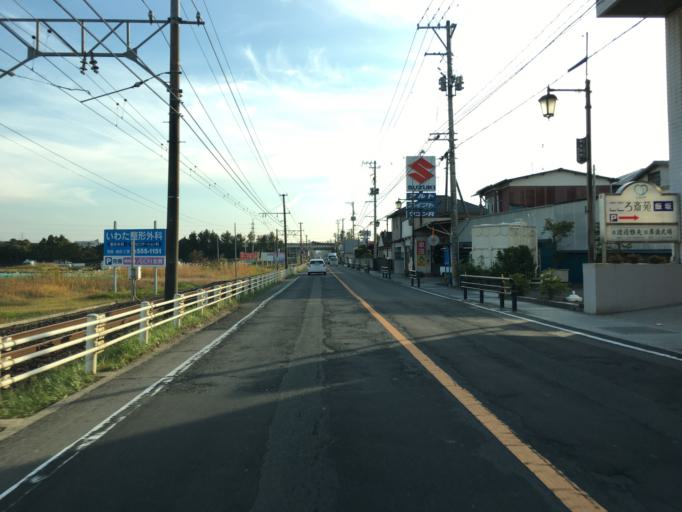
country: JP
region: Fukushima
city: Fukushima-shi
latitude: 37.8036
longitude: 140.4423
